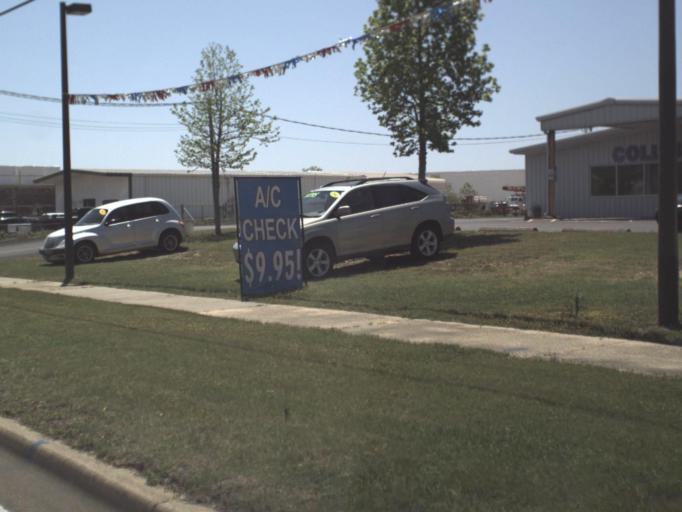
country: US
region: Florida
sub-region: Escambia County
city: Bellview
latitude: 30.4791
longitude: -87.3068
